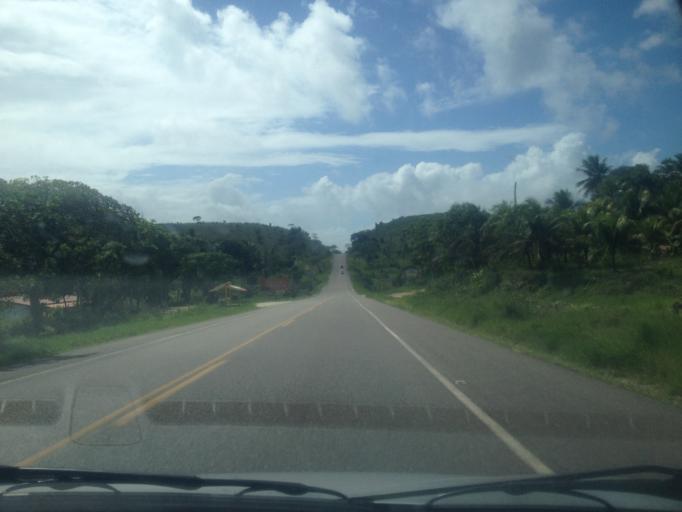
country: BR
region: Bahia
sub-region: Conde
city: Conde
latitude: -11.7839
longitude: -37.6164
